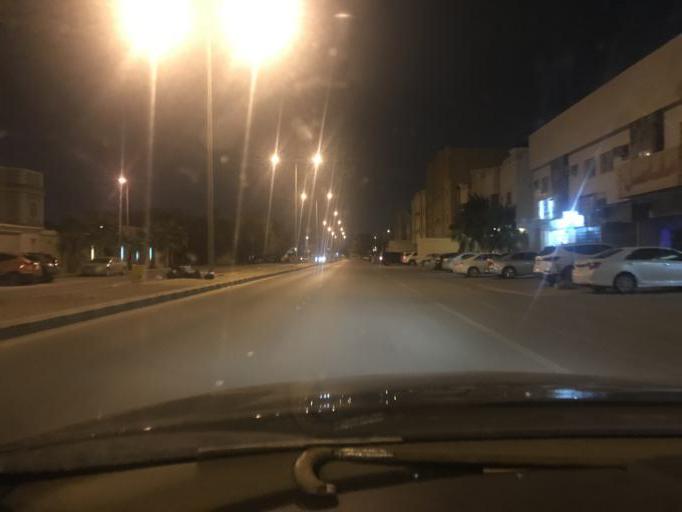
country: SA
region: Ar Riyad
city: Riyadh
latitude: 24.7515
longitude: 46.7746
